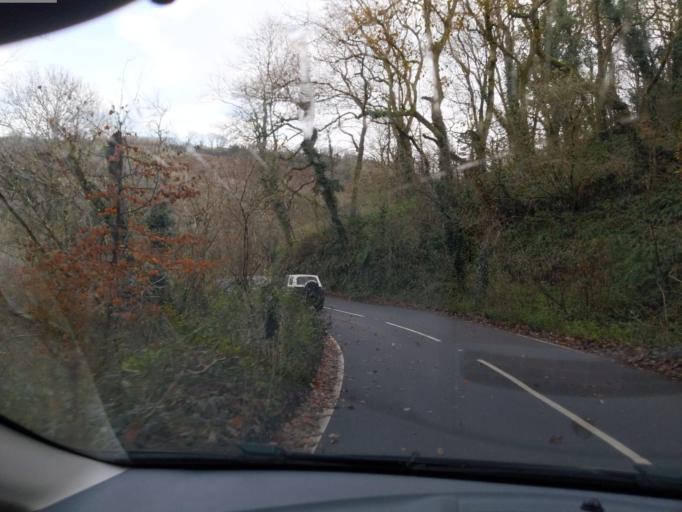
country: GB
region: England
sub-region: Cornwall
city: Looe
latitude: 50.3726
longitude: -4.3881
